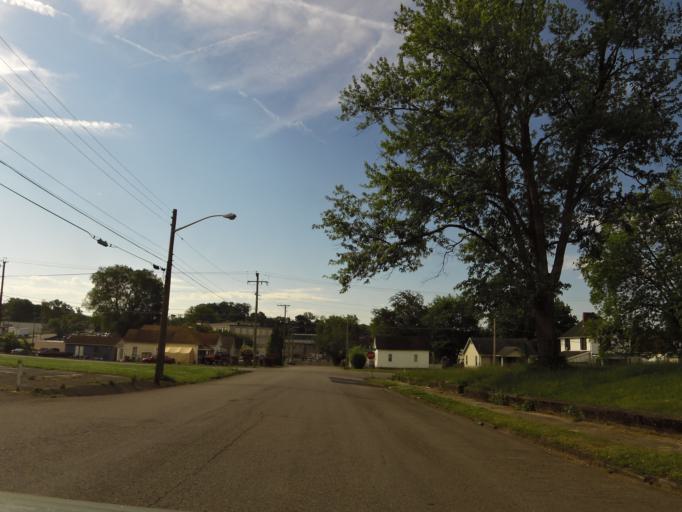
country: US
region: Tennessee
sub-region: Knox County
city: Knoxville
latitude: 35.9909
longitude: -83.9137
